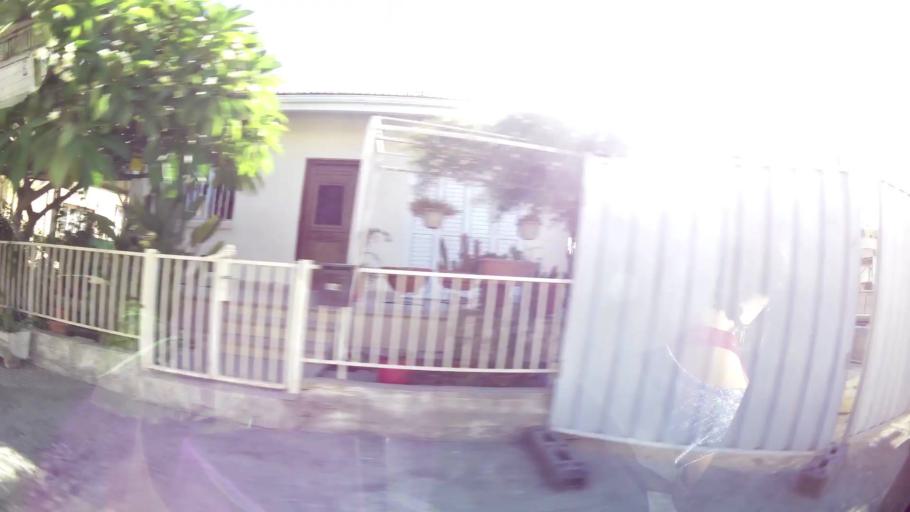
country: CY
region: Larnaka
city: Larnaca
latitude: 34.9320
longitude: 33.6248
